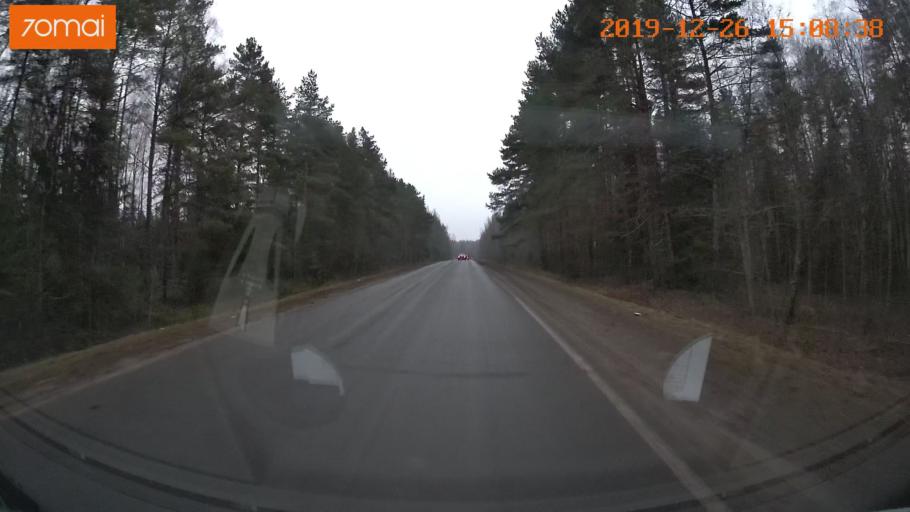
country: RU
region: Jaroslavl
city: Rybinsk
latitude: 58.1578
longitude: 38.8370
